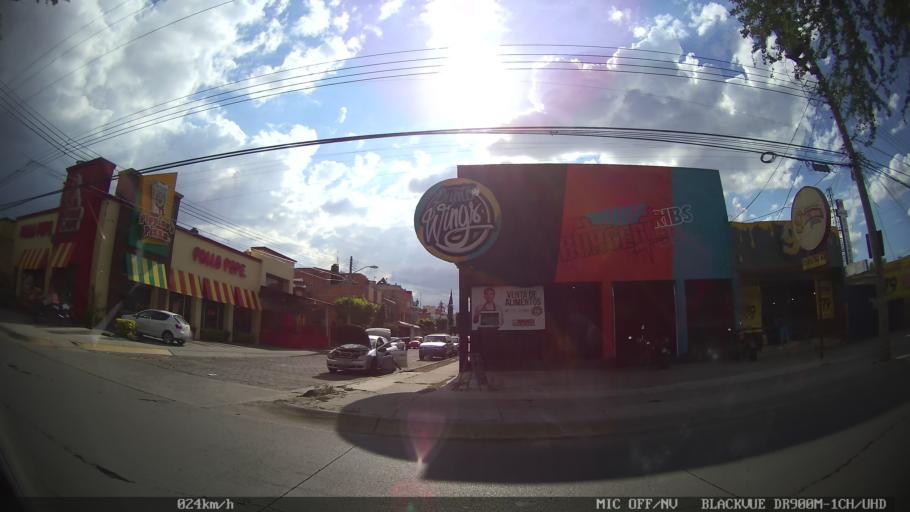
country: MX
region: Jalisco
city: Tlaquepaque
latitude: 20.6367
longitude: -103.2839
